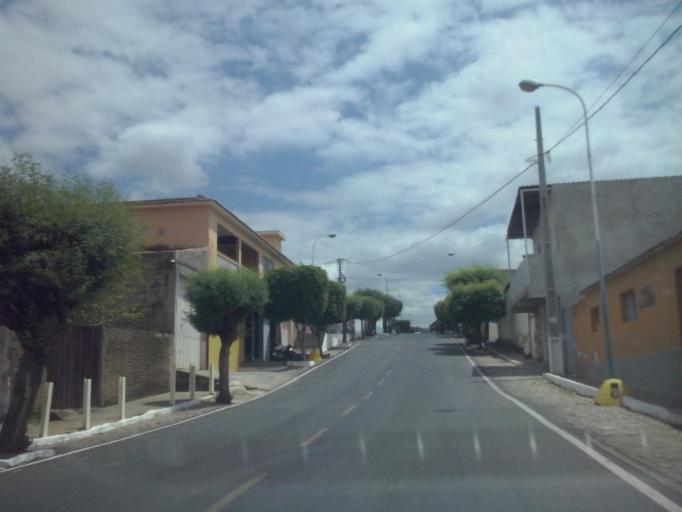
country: BR
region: Paraiba
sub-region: Patos
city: Patos
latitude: -6.9058
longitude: -37.5196
